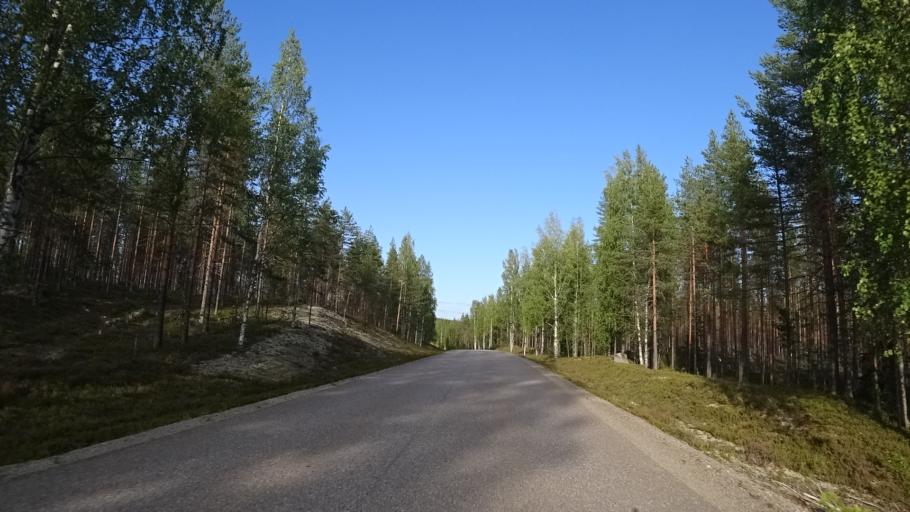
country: FI
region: North Karelia
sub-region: Joensuu
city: Eno
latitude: 63.0282
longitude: 30.5163
